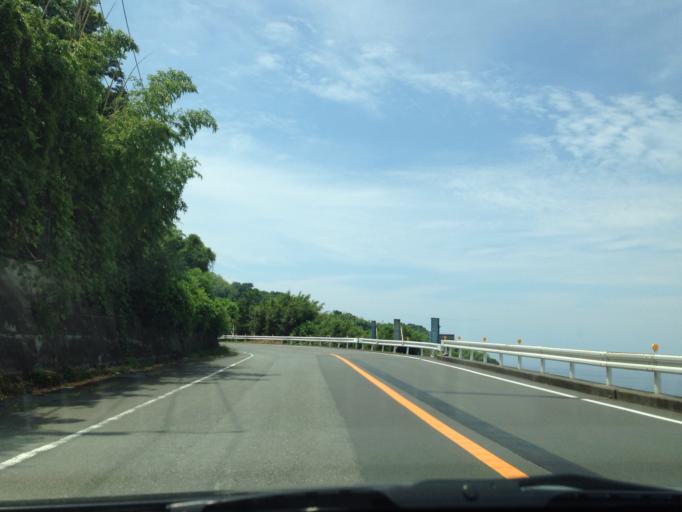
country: JP
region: Shizuoka
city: Heda
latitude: 34.8947
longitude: 138.7663
